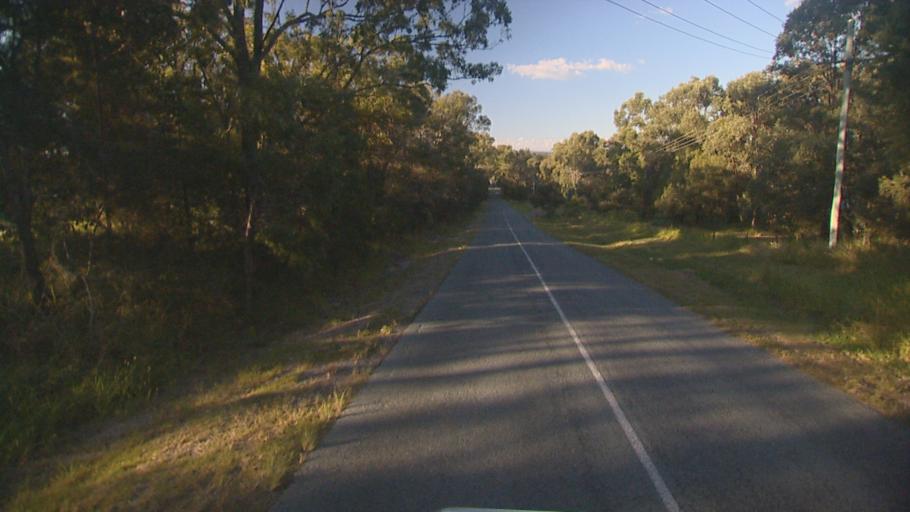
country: AU
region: Queensland
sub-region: Logan
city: Logan Reserve
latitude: -27.7238
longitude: 153.1058
